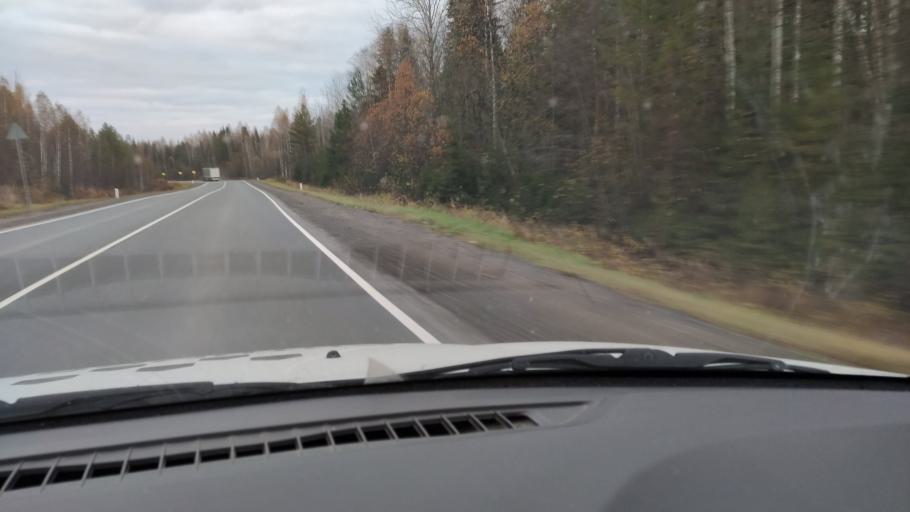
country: RU
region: Kirov
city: Belorechensk
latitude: 58.7571
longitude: 52.3510
